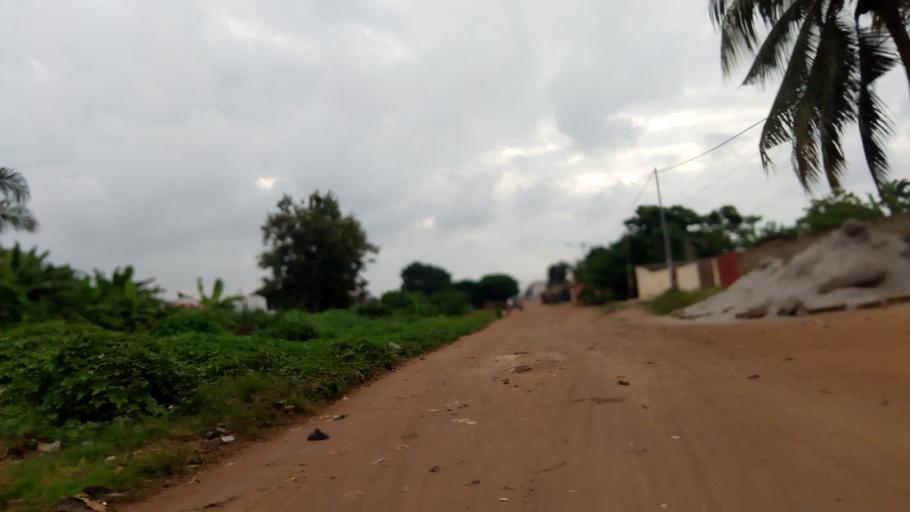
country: TG
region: Maritime
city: Lome
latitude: 6.1744
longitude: 1.1934
